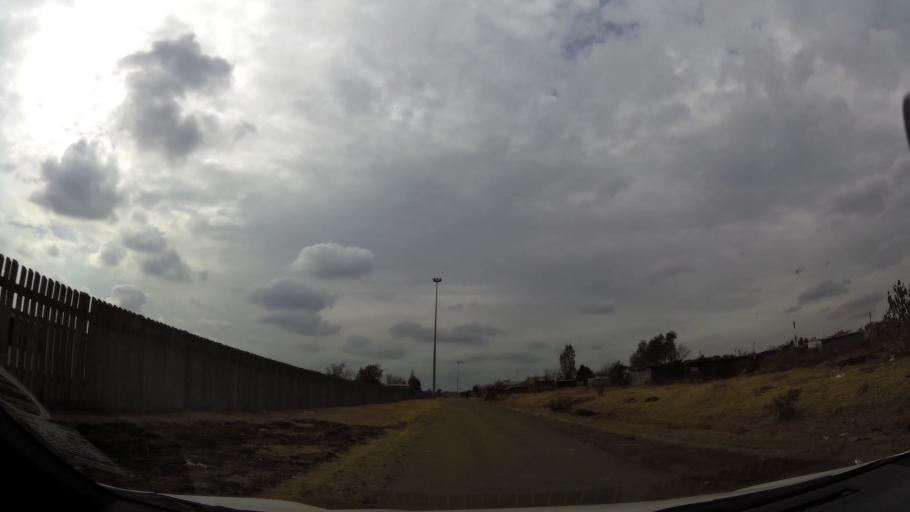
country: ZA
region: Gauteng
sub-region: Ekurhuleni Metropolitan Municipality
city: Germiston
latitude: -26.3916
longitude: 28.1227
